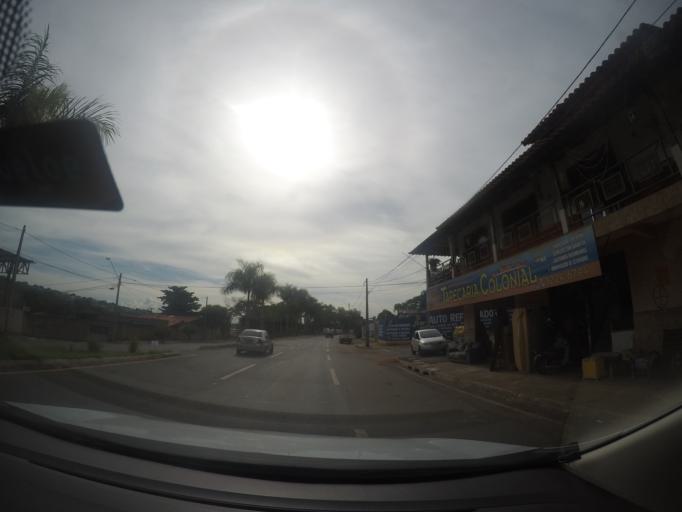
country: BR
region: Goias
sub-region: Goiania
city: Goiania
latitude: -16.6555
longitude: -49.3015
